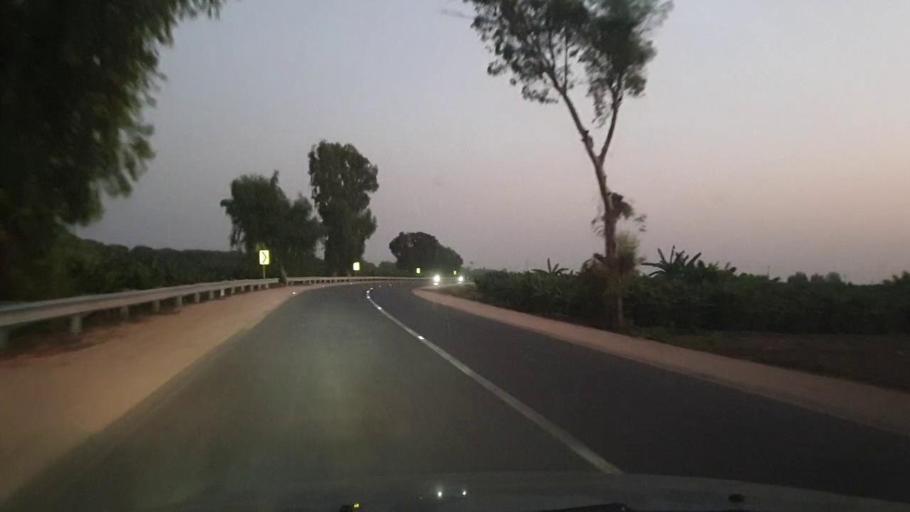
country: PK
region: Sindh
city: Tando Allahyar
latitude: 25.4187
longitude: 68.7550
